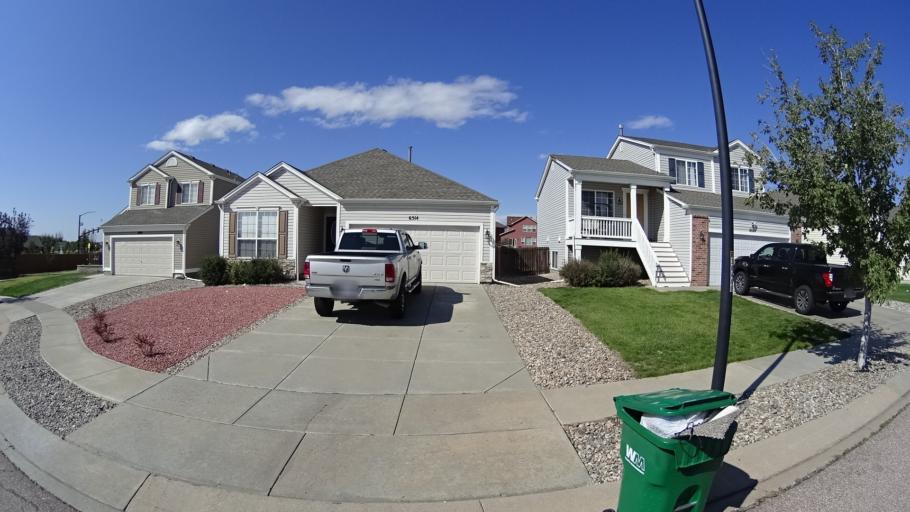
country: US
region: Colorado
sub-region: El Paso County
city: Cimarron Hills
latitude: 38.9270
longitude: -104.6986
